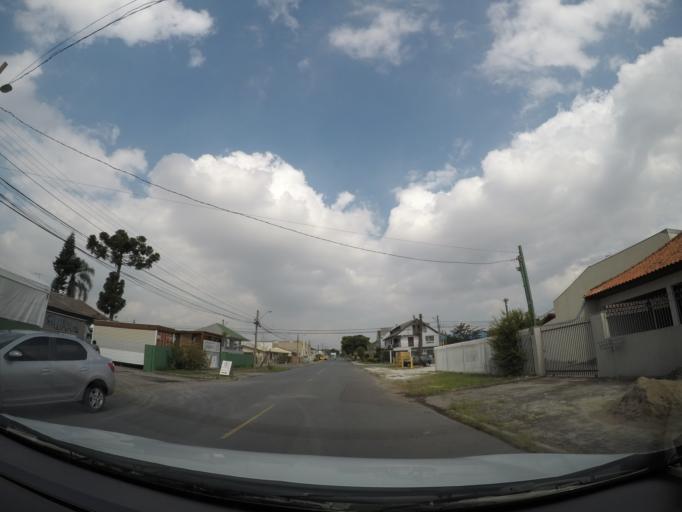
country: BR
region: Parana
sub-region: Curitiba
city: Curitiba
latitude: -25.4790
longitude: -49.2539
